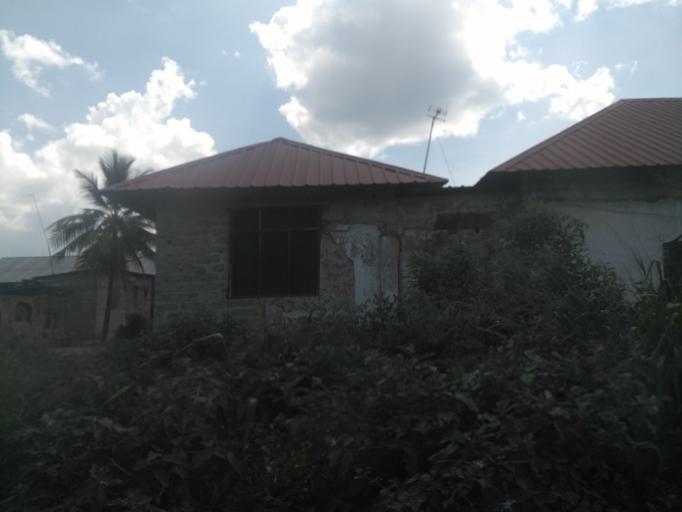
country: TZ
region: Zanzibar Urban/West
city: Zanzibar
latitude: -6.1704
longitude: 39.2106
